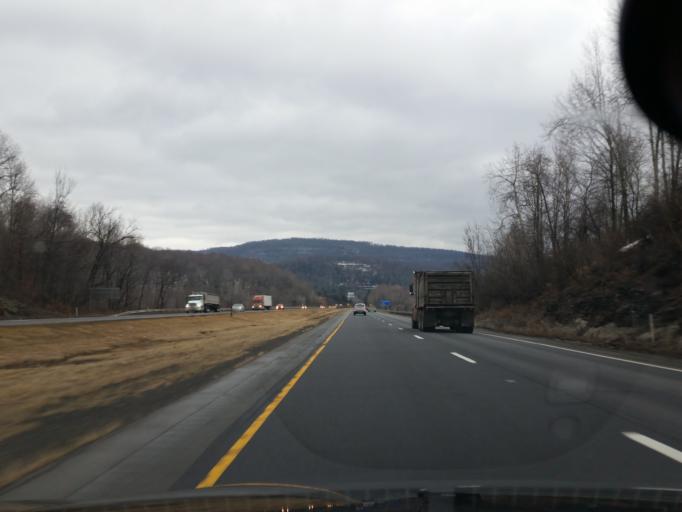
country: US
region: Pennsylvania
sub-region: Lackawanna County
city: Dalton
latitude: 41.6602
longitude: -75.6720
